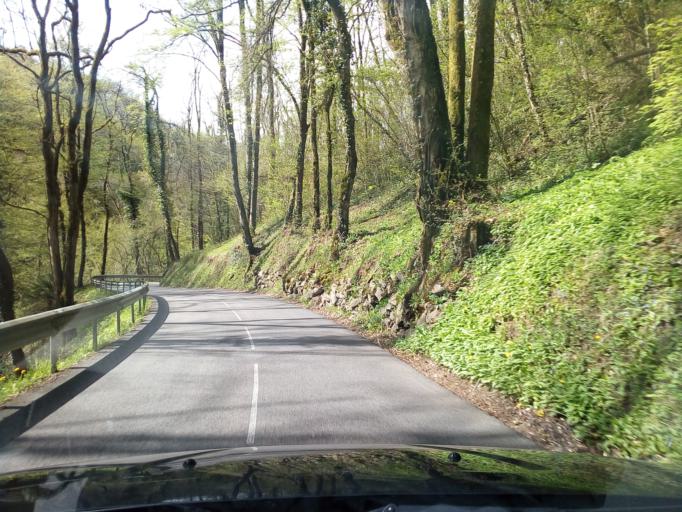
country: FR
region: Rhone-Alpes
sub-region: Departement de l'Isere
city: Gieres
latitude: 45.1641
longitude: 5.8259
